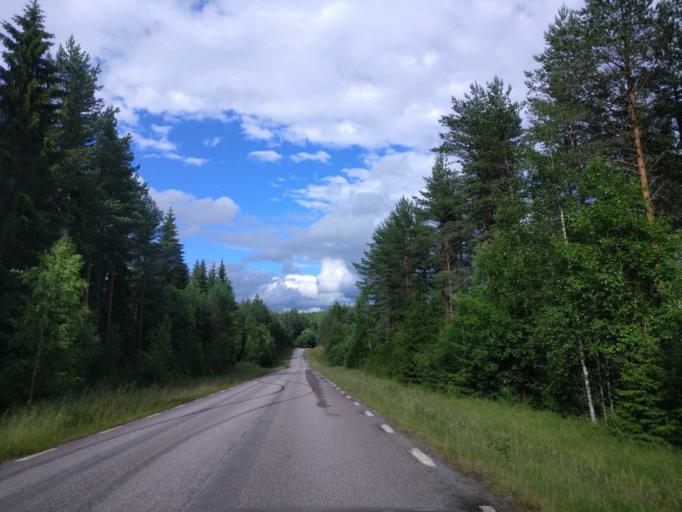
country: SE
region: Vaermland
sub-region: Hagfors Kommun
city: Ekshaerad
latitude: 60.0422
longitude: 13.5183
